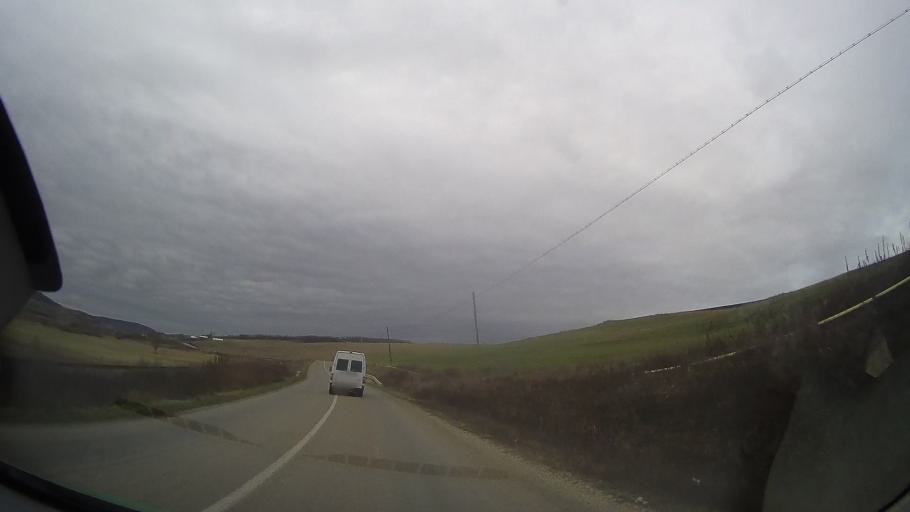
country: RO
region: Cluj
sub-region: Comuna Catina
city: Catina
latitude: 46.8065
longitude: 24.2165
